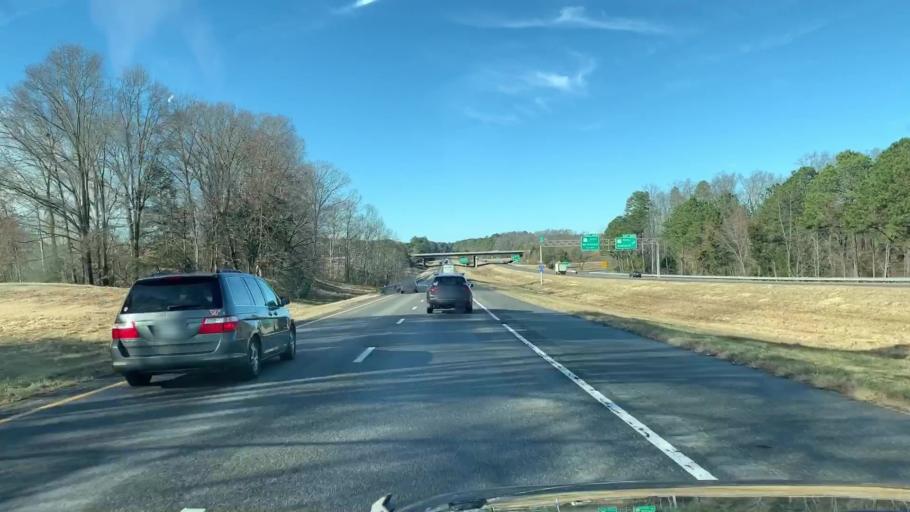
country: US
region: Virginia
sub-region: Henrico County
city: Chamberlayne
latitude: 37.6584
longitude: -77.4543
